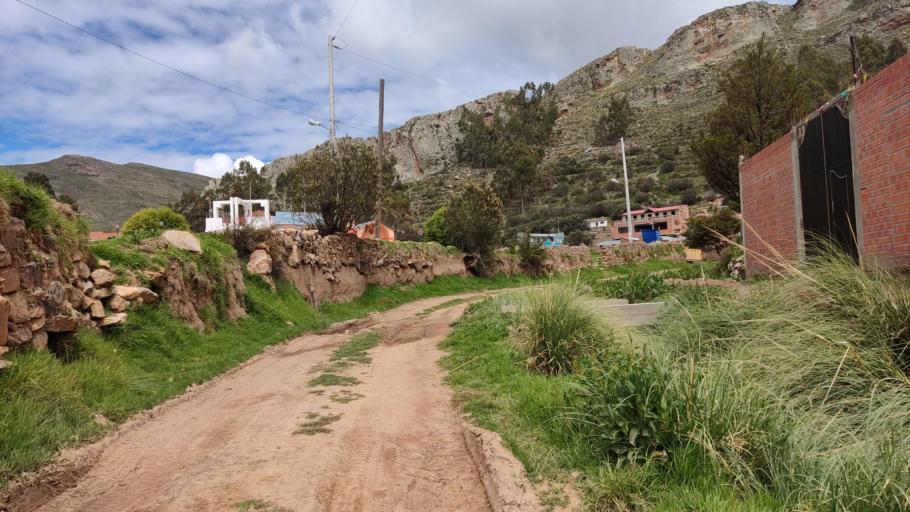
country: BO
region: La Paz
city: Batallas
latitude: -16.3469
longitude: -68.6388
